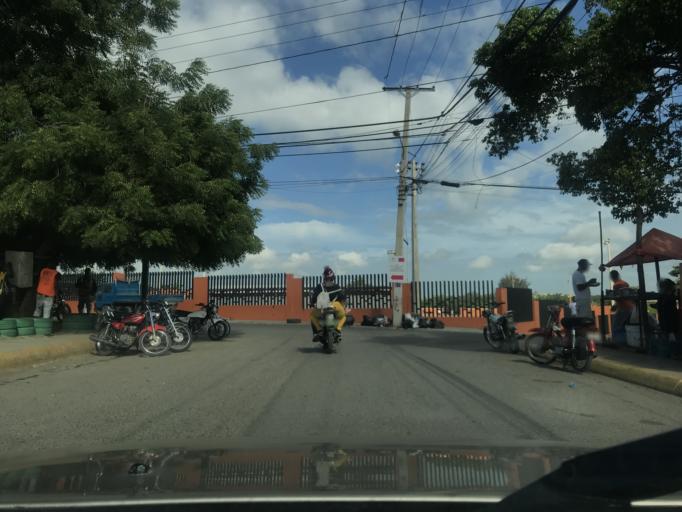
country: DO
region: Santiago
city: Palmar Arriba
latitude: 19.4853
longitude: -70.7475
